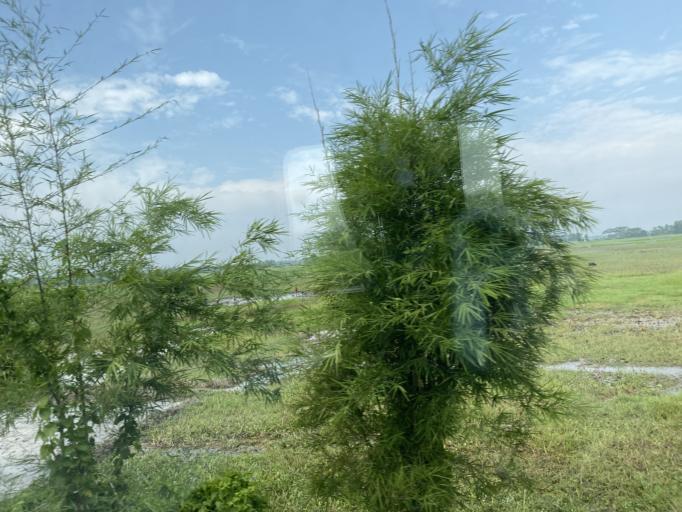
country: IN
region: Tripura
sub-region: West Tripura
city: Agartala
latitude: 23.9935
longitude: 91.2867
